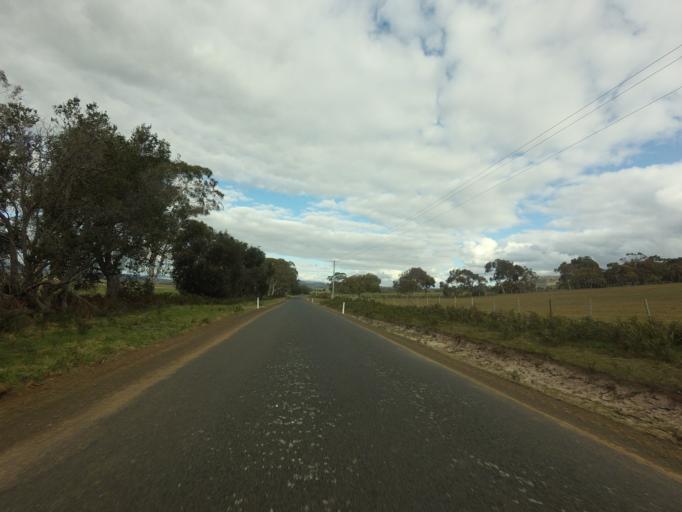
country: AU
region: Tasmania
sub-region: Northern Midlands
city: Evandale
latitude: -41.8735
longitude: 147.3005
